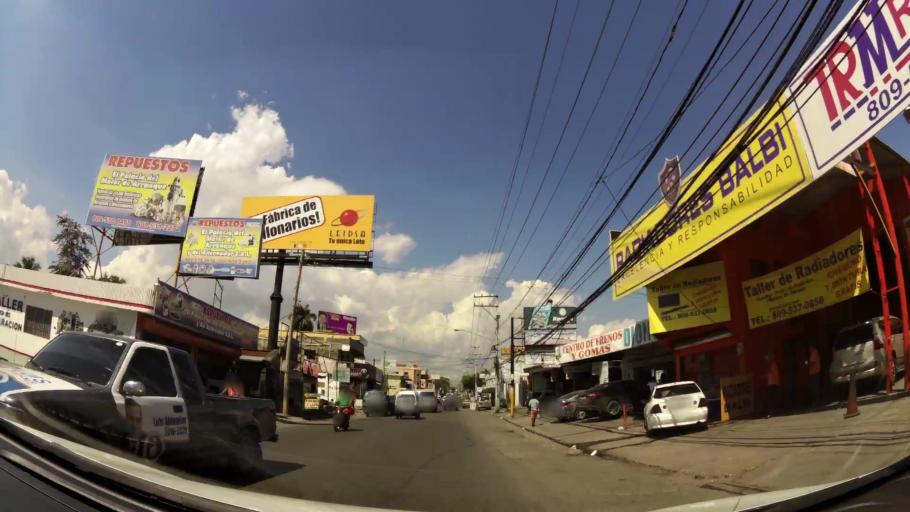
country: DO
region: Nacional
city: Bella Vista
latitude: 18.4613
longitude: -69.9762
